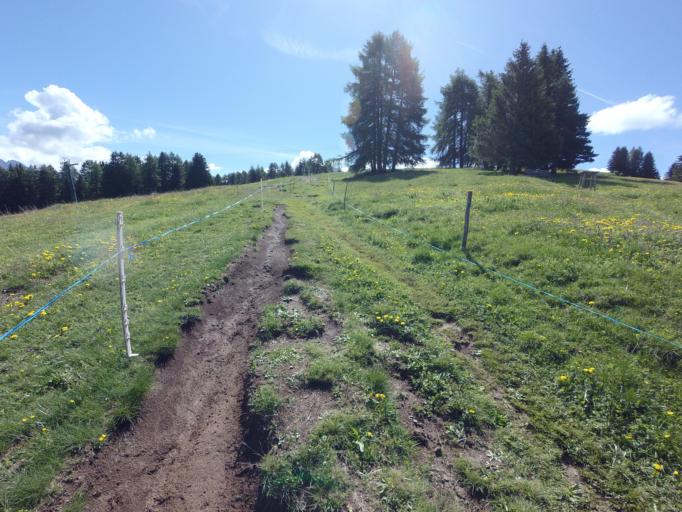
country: IT
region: Trentino-Alto Adige
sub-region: Bolzano
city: Ortisei
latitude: 46.5383
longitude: 11.6353
